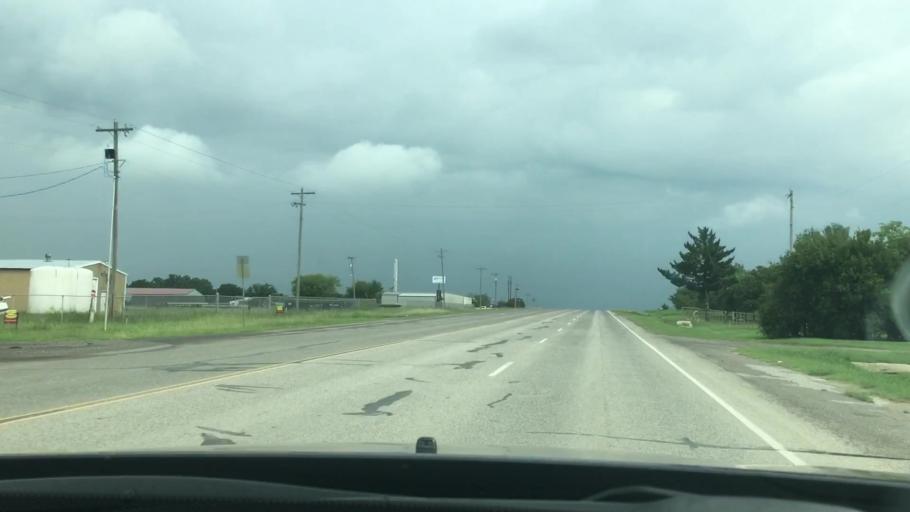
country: US
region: Oklahoma
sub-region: Carter County
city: Wilson
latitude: 34.1769
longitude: -97.4747
